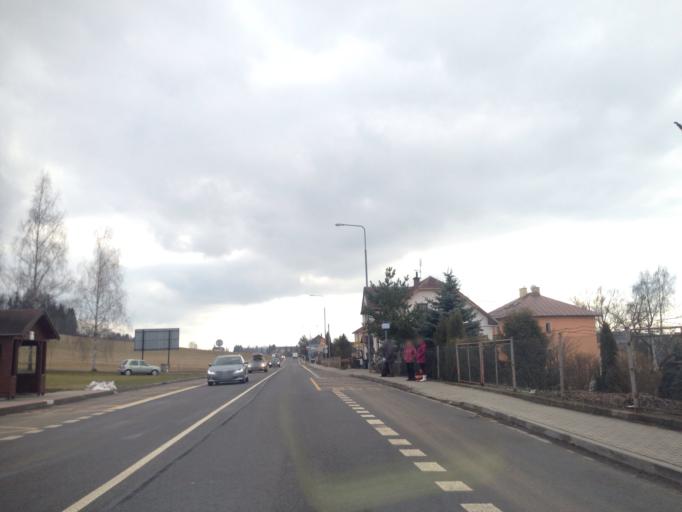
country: CZ
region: Liberecky
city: Studenec
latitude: 50.5635
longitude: 15.5450
